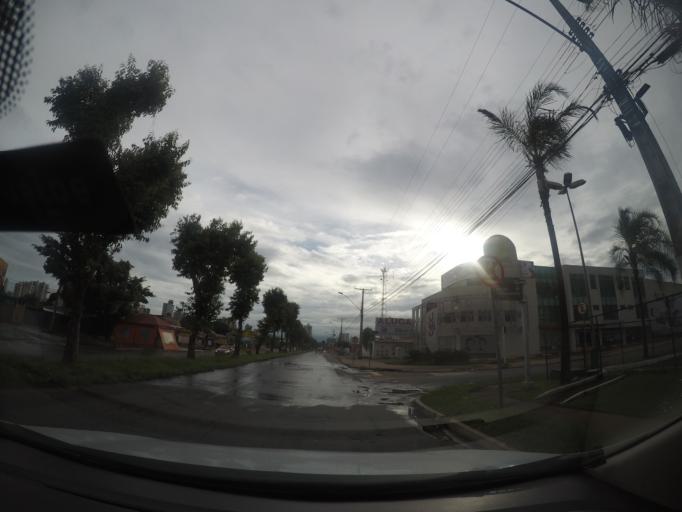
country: BR
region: Goias
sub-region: Goiania
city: Goiania
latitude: -16.7406
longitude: -49.2783
